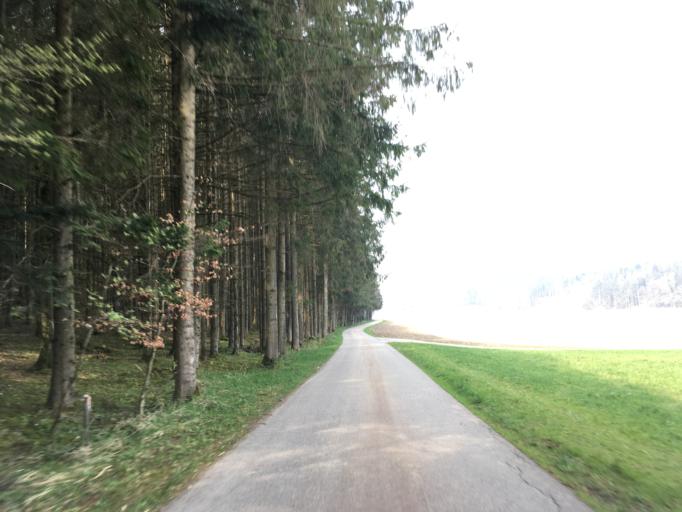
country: DE
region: Bavaria
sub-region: Upper Bavaria
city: Jettenbach
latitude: 48.1546
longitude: 12.3800
